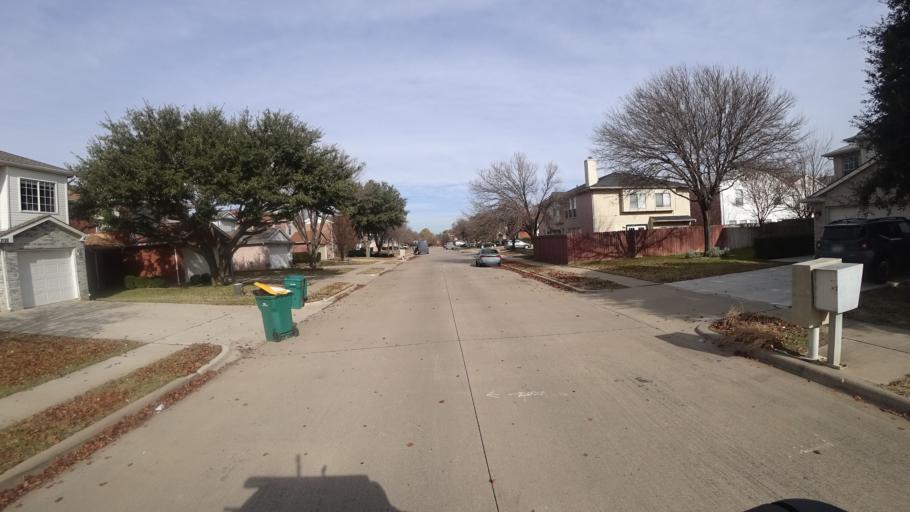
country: US
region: Texas
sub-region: Denton County
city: Highland Village
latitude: 33.0744
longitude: -97.0319
